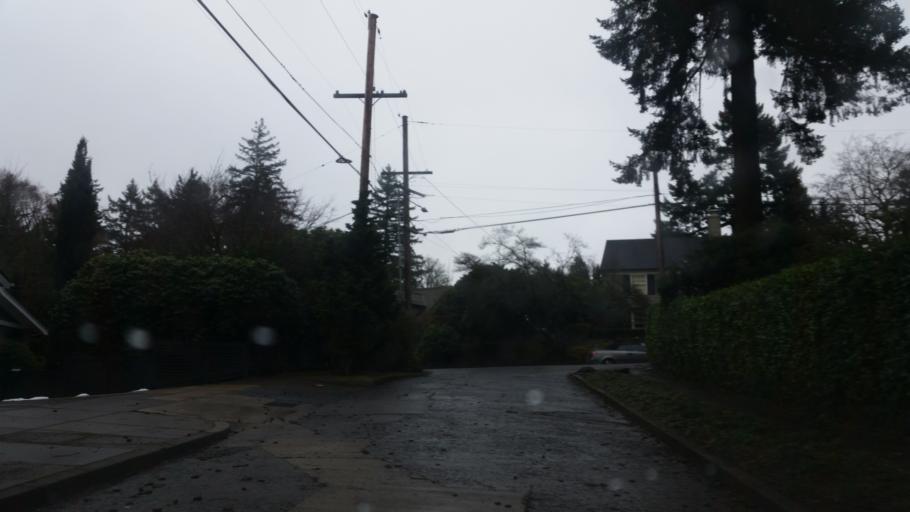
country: US
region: Oregon
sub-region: Multnomah County
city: Portland
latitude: 45.5060
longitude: -122.7056
